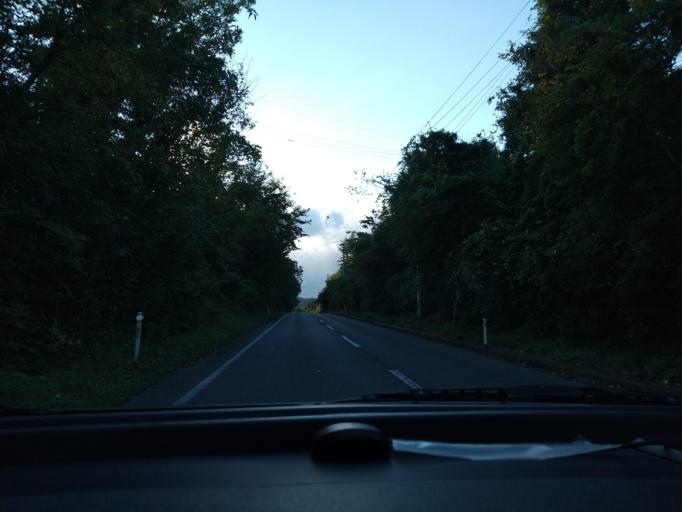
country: JP
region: Iwate
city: Ichinoseki
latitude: 38.9718
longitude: 141.2161
